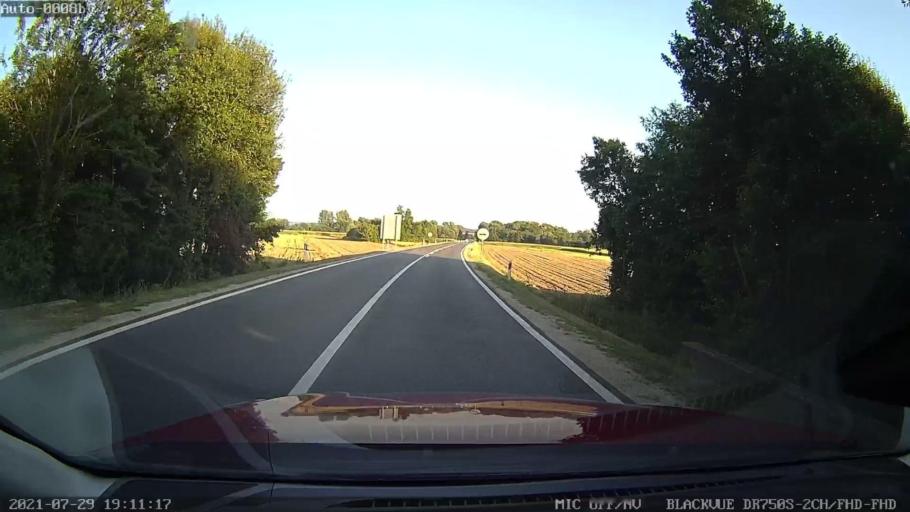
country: HR
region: Varazdinska
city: Jalzabet
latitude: 46.2802
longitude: 16.5078
